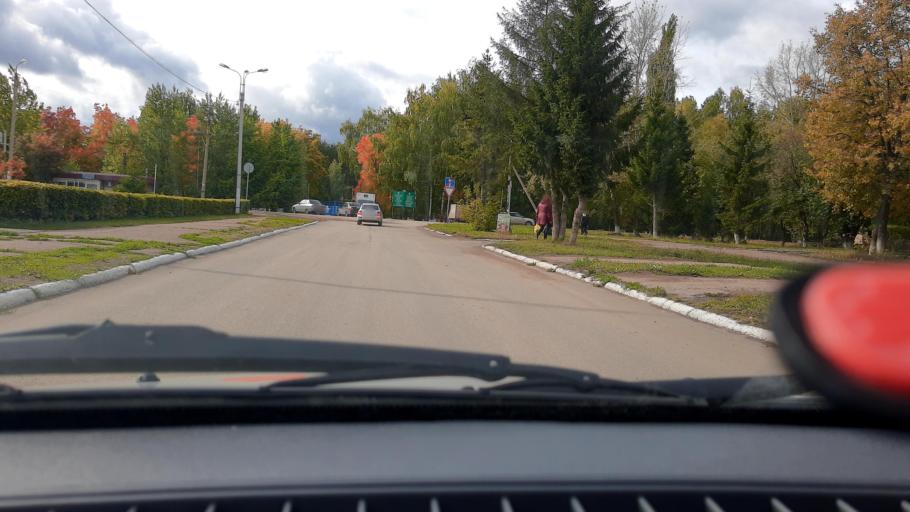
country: RU
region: Bashkortostan
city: Belebey
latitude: 54.1029
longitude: 54.0978
